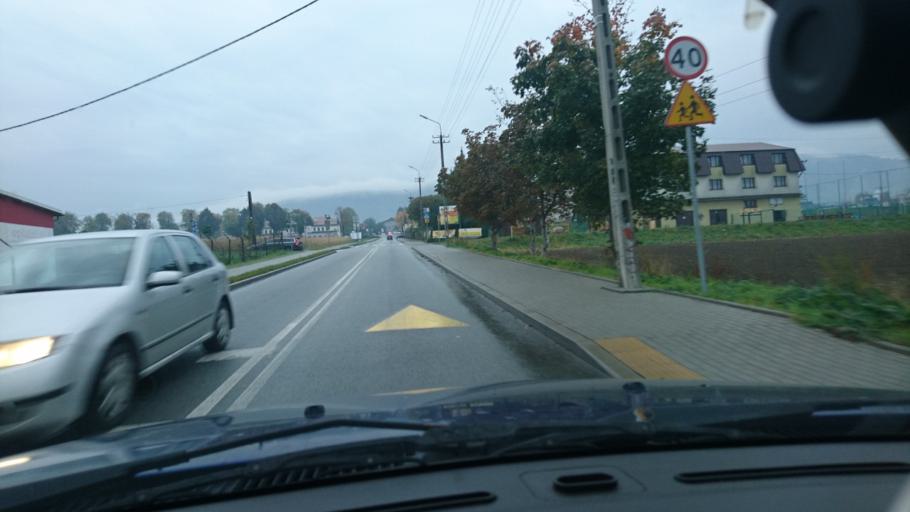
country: PL
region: Silesian Voivodeship
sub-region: Powiat bielski
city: Kozy
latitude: 49.8493
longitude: 19.1451
